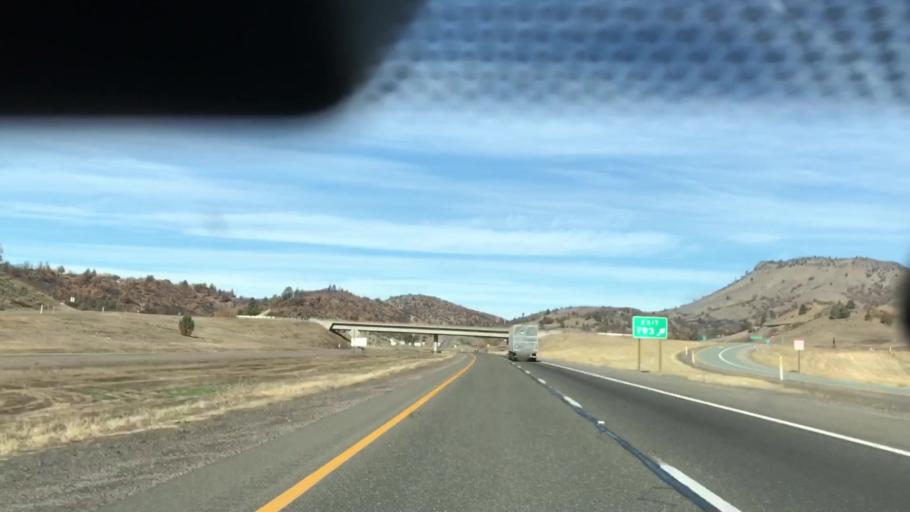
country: US
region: California
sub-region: Siskiyou County
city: Yreka
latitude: 41.9526
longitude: -122.5907
